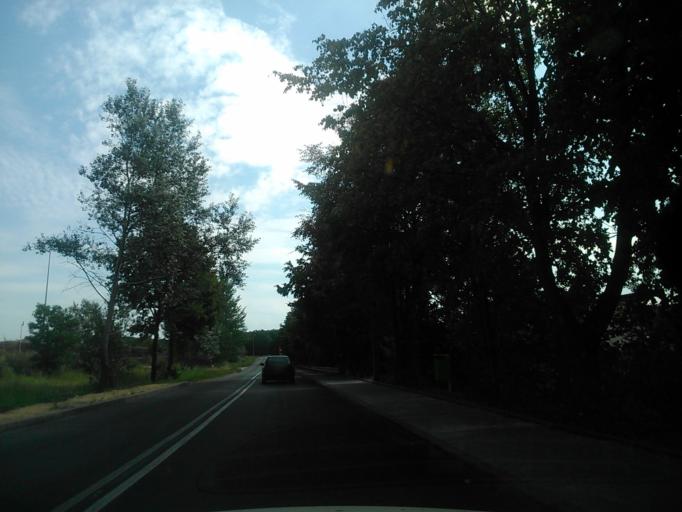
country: PL
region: Warmian-Masurian Voivodeship
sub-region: Powiat dzialdowski
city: Ilowo -Osada
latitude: 53.1626
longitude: 20.2973
